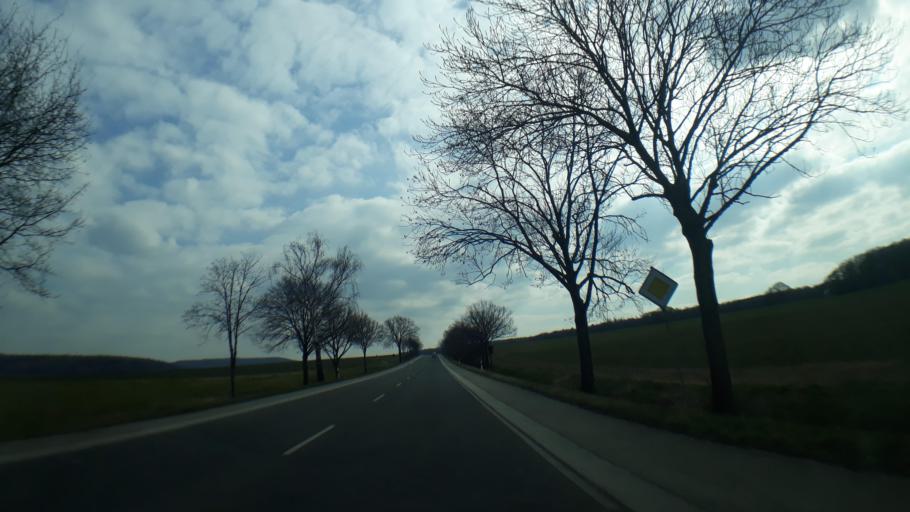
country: DE
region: North Rhine-Westphalia
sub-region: Regierungsbezirk Koln
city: Rheinbach
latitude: 50.6048
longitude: 6.8626
